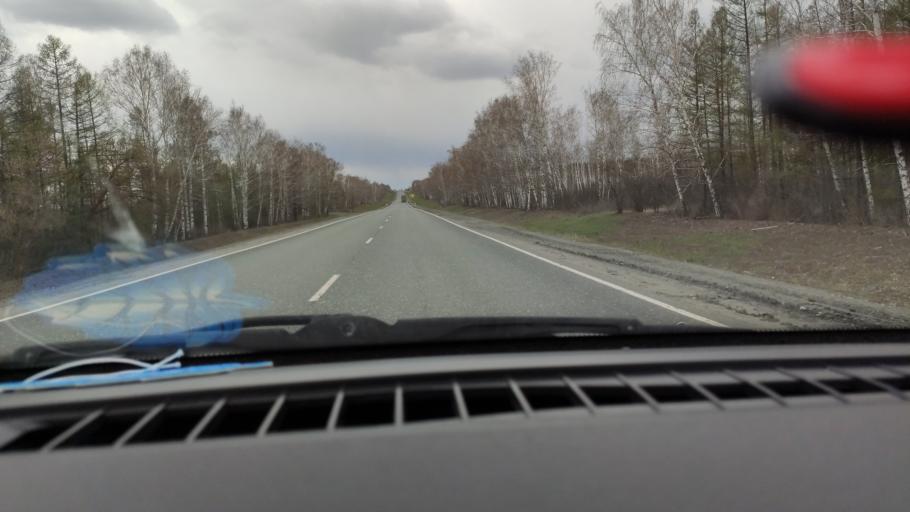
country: RU
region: Saratov
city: Sennoy
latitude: 52.1224
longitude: 46.8482
